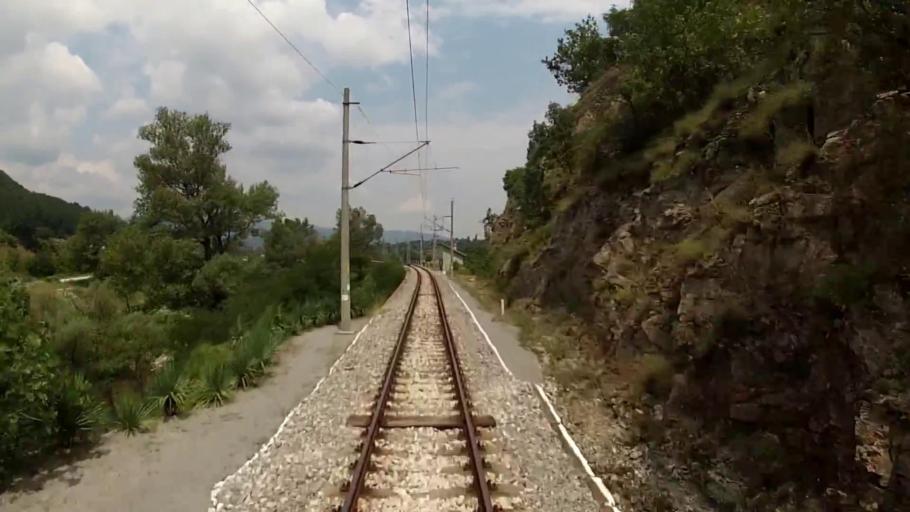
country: BG
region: Blagoevgrad
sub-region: Obshtina Kresna
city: Stara Kresna
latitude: 41.8362
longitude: 23.1552
